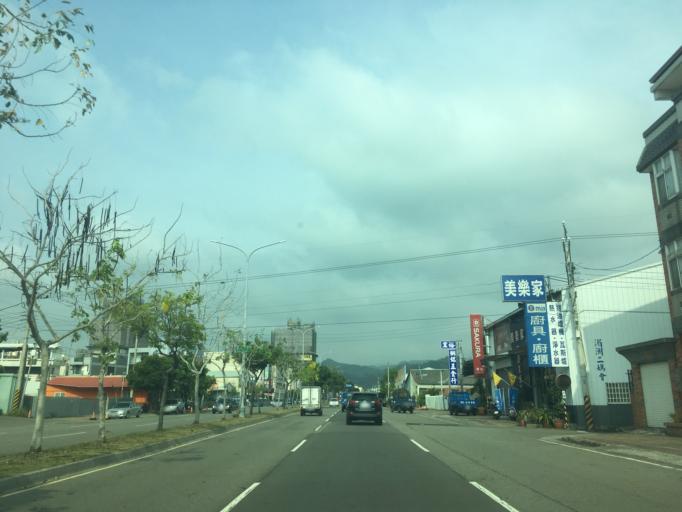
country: TW
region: Taiwan
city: Fengyuan
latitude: 24.2368
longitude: 120.7155
